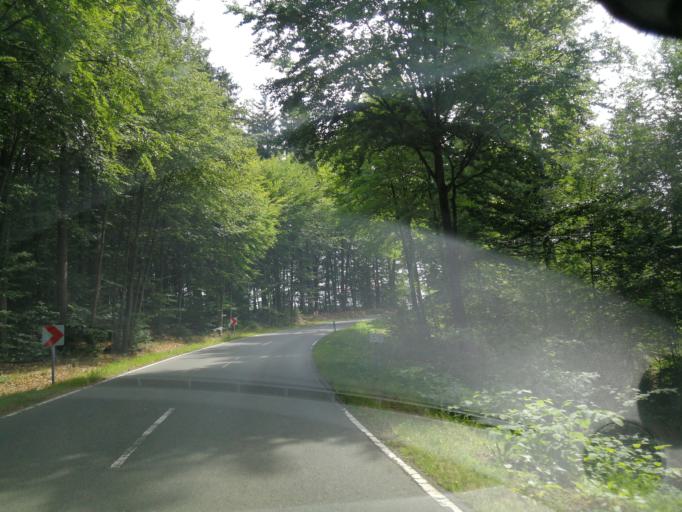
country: DE
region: Bavaria
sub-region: Upper Palatinate
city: Falkenstein
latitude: 49.0902
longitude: 12.4917
